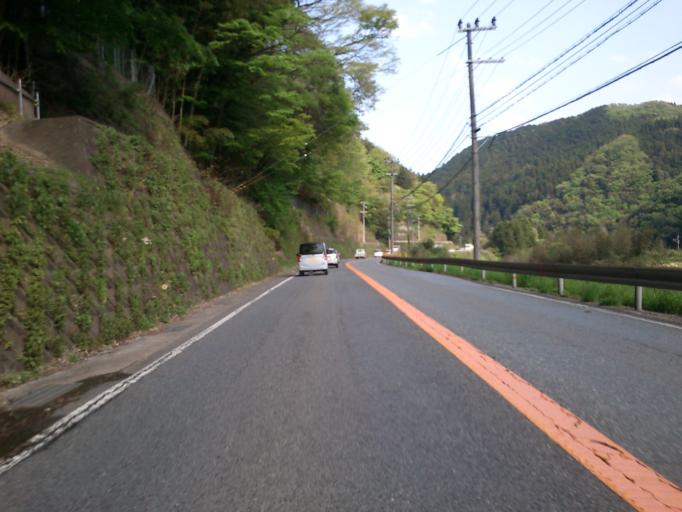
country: JP
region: Kyoto
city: Fukuchiyama
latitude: 35.3220
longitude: 134.9809
